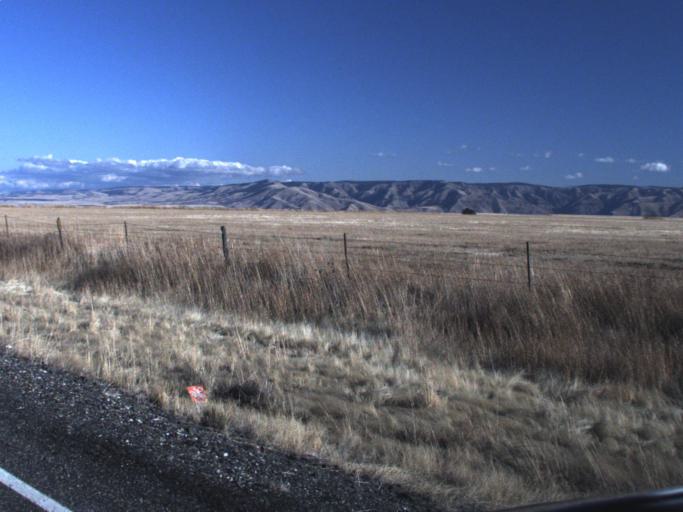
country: US
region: Washington
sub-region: Asotin County
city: Asotin
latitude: 46.1530
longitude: -117.1159
